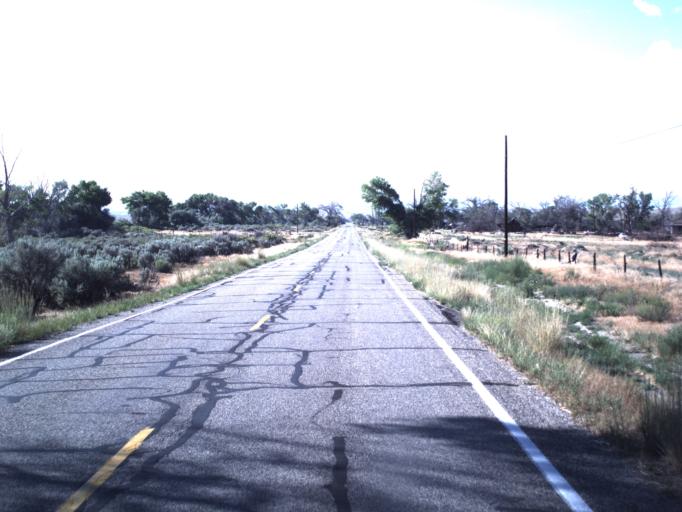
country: US
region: Utah
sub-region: Emery County
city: Huntington
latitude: 39.4148
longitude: -110.8558
